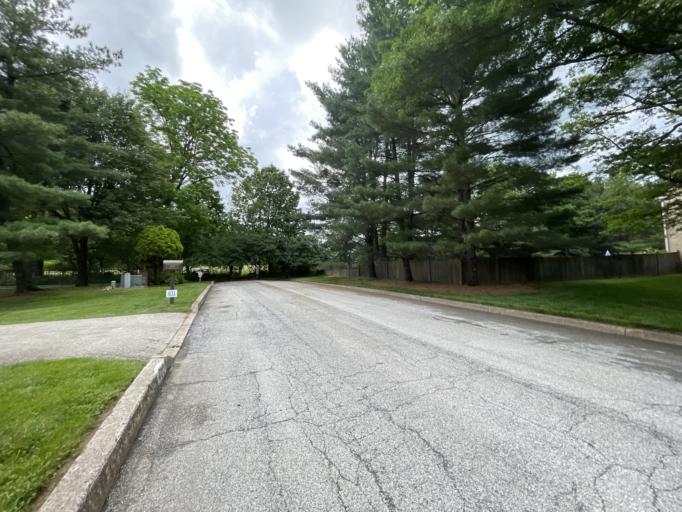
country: US
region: Pennsylvania
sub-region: Montgomery County
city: Blue Bell
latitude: 40.1548
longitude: -75.2521
